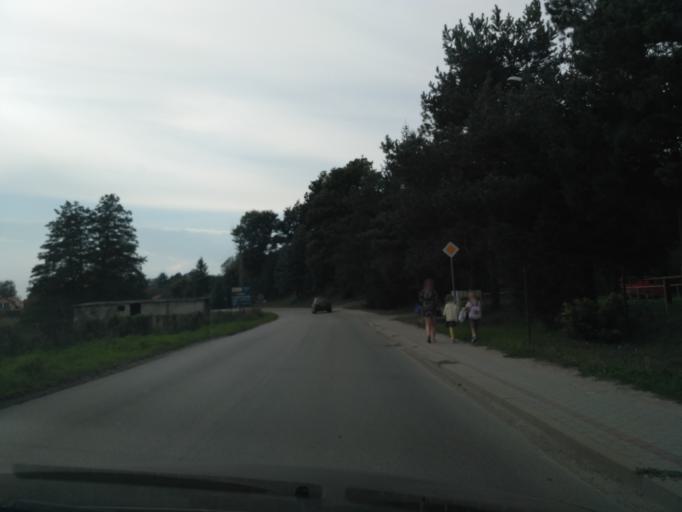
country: PL
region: Subcarpathian Voivodeship
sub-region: Powiat rzeszowski
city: Zglobien
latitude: 50.0122
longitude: 21.8559
